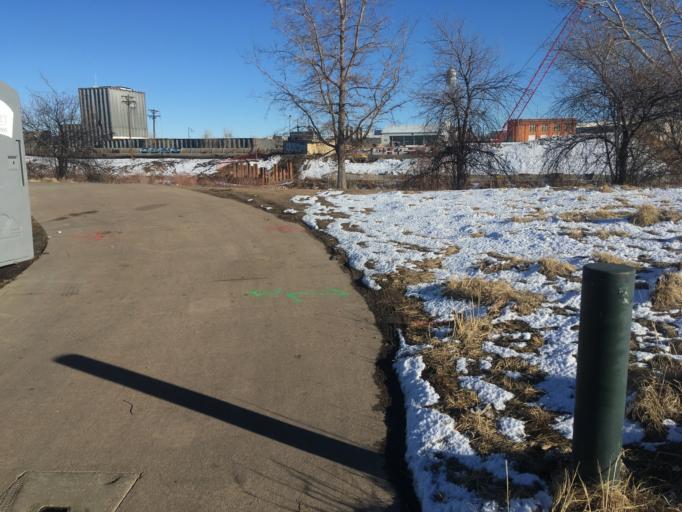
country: US
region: Colorado
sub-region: Adams County
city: Commerce City
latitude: 39.7880
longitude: -104.9740
